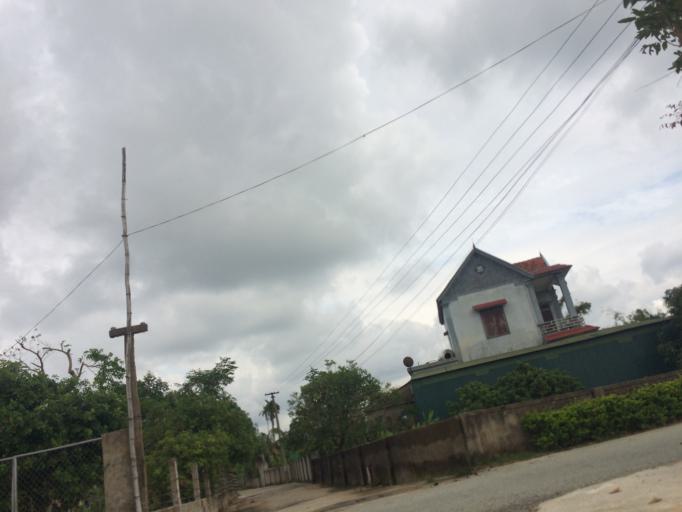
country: VN
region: Ha Tinh
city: Ha Tinh
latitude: 18.3407
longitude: 105.9322
